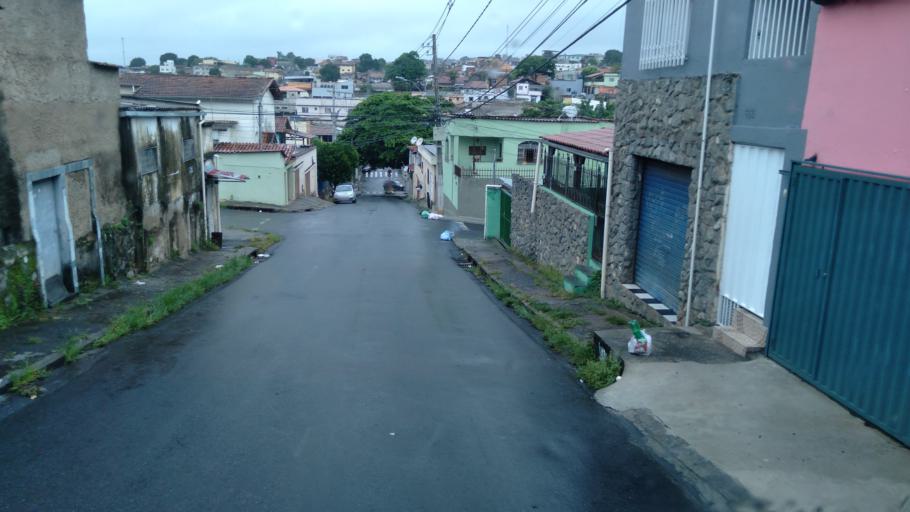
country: BR
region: Minas Gerais
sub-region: Belo Horizonte
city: Belo Horizonte
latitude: -19.9139
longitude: -43.9022
